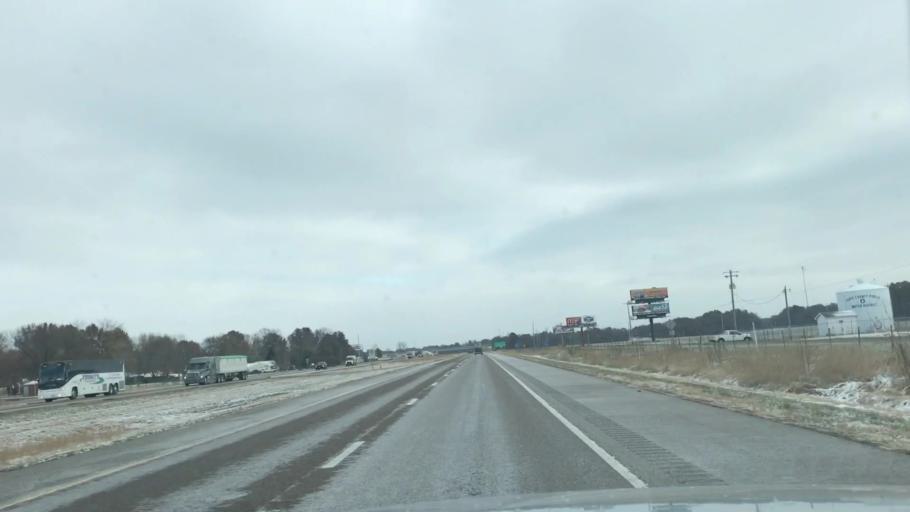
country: US
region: Illinois
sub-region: Macoupin County
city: Staunton
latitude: 38.9607
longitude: -89.7623
